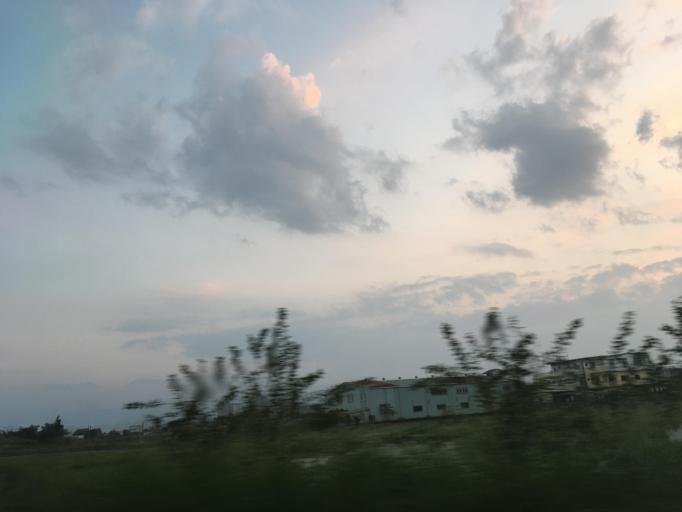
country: TW
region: Taiwan
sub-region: Yilan
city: Yilan
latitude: 24.6923
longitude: 121.7819
